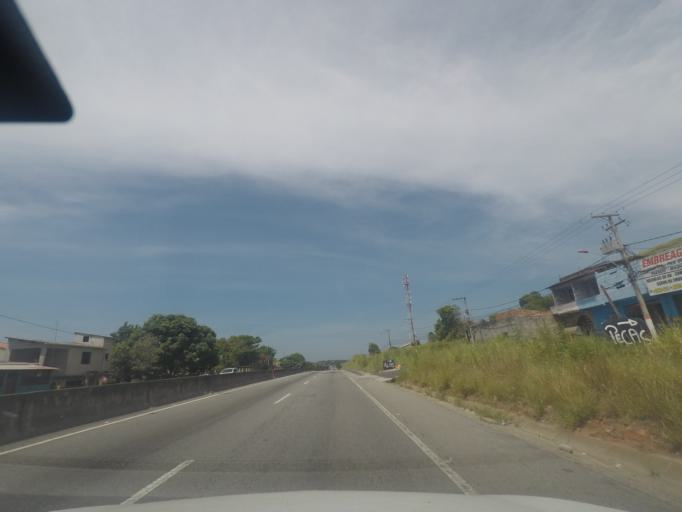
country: BR
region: Rio de Janeiro
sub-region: Marica
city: Marica
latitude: -22.9212
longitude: -42.8575
